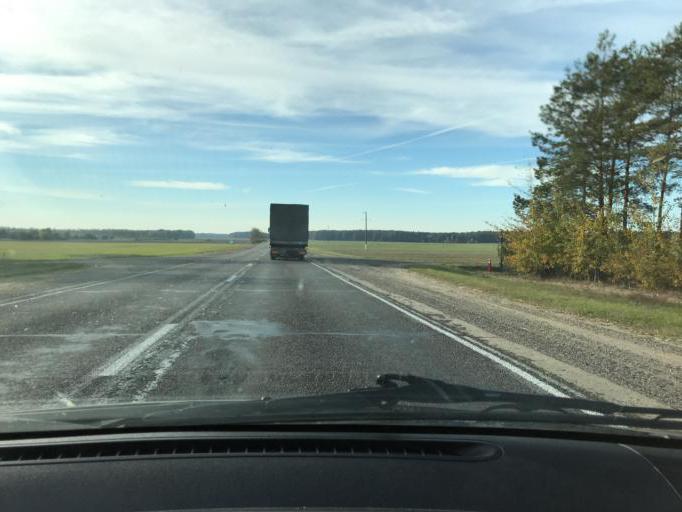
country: BY
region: Brest
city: Lahishyn
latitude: 52.1524
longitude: 25.8300
